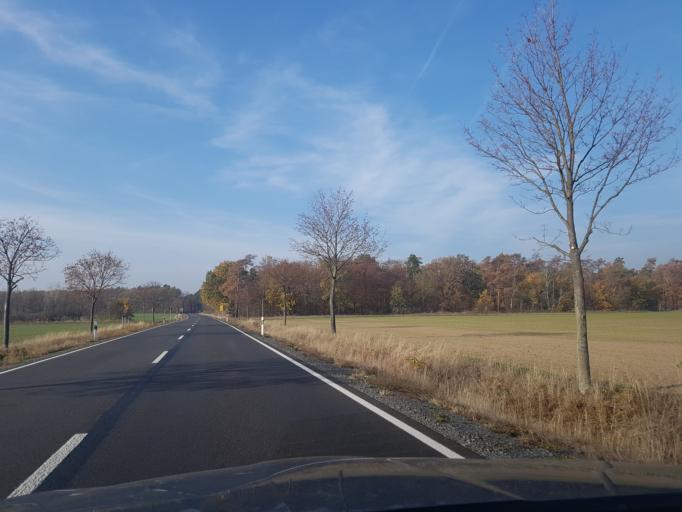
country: DE
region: Saxony
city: Arzberg
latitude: 51.5511
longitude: 13.1380
